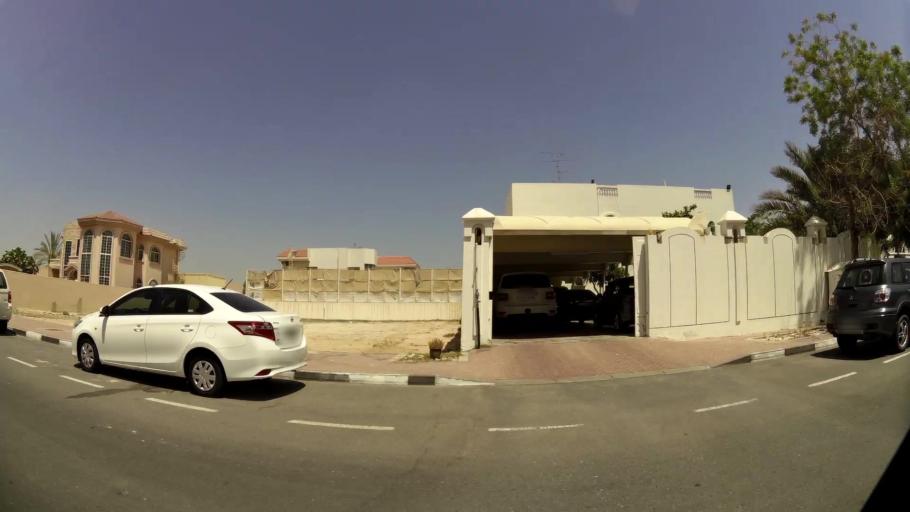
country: AE
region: Dubai
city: Dubai
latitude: 25.2125
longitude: 55.2701
